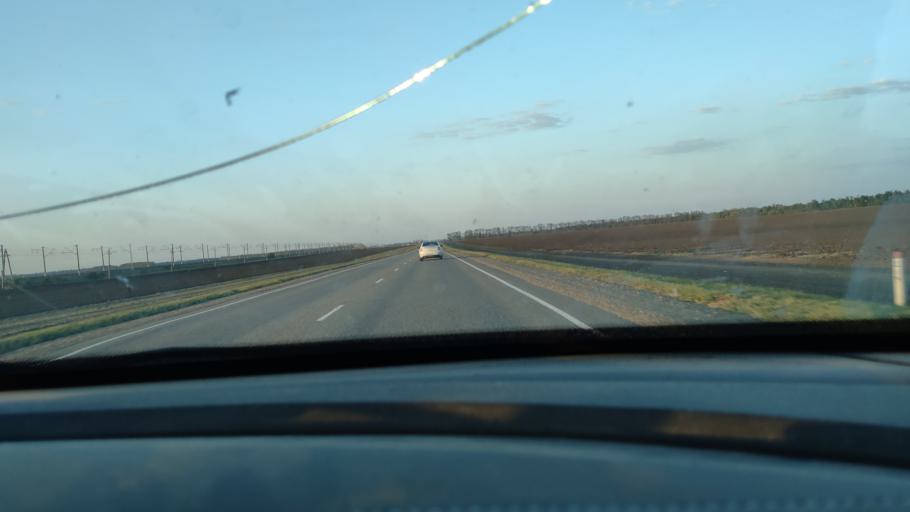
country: RU
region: Krasnodarskiy
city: Novominskaya
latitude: 46.3387
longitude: 38.9506
